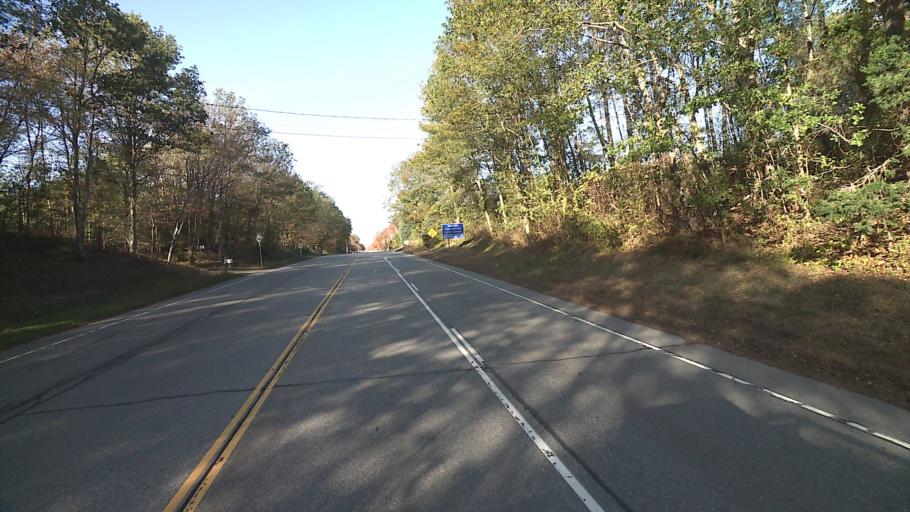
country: US
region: Connecticut
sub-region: Windham County
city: Killingly Center
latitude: 41.7908
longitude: -71.8129
